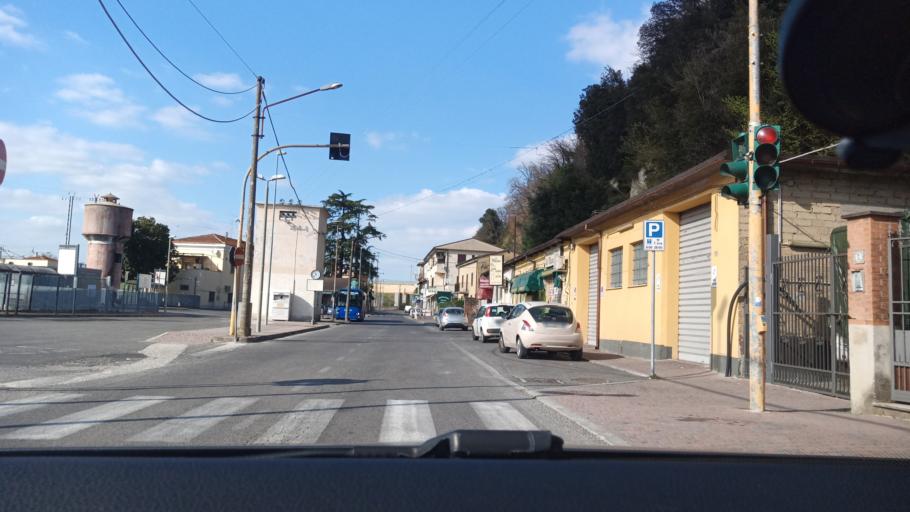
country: IT
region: Latium
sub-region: Citta metropolitana di Roma Capitale
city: Torrita Tiberina
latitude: 42.2412
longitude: 12.6338
